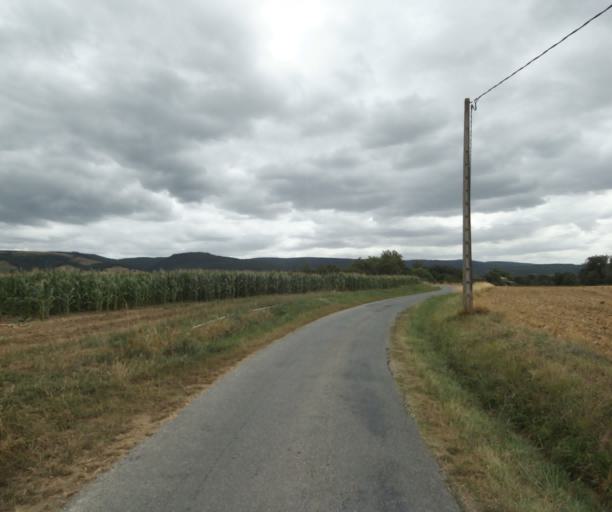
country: FR
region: Midi-Pyrenees
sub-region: Departement du Tarn
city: Soreze
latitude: 43.4707
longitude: 2.0666
